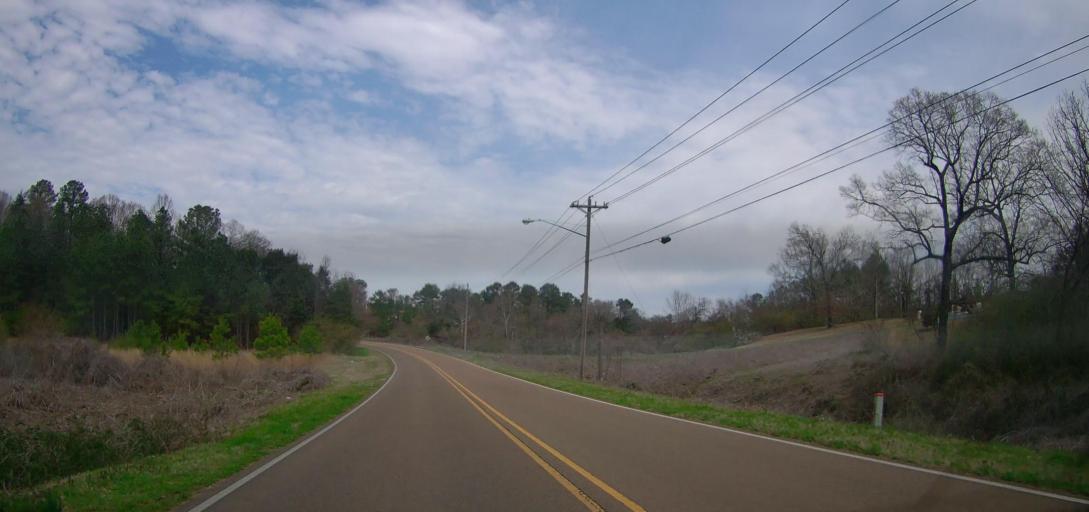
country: US
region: Mississippi
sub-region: Marshall County
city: Holly Springs
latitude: 34.7565
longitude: -89.4294
